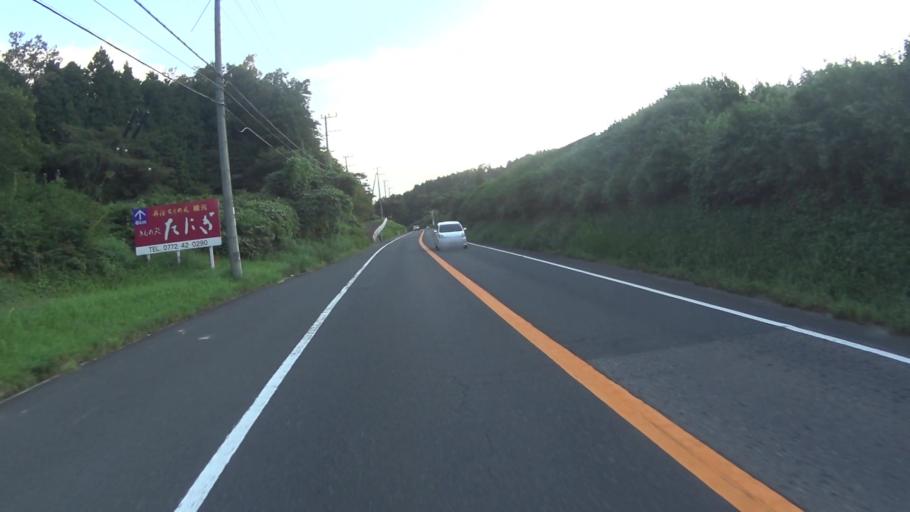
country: JP
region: Kyoto
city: Miyazu
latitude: 35.5576
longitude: 135.1125
